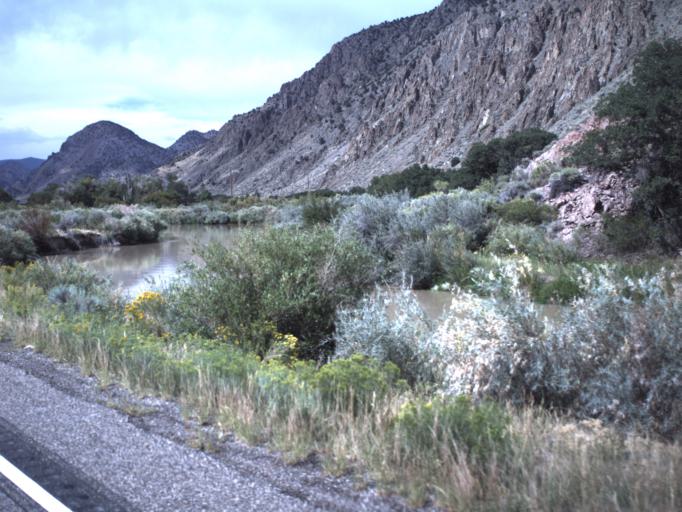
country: US
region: Utah
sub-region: Sevier County
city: Monroe
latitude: 38.4977
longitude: -112.2565
